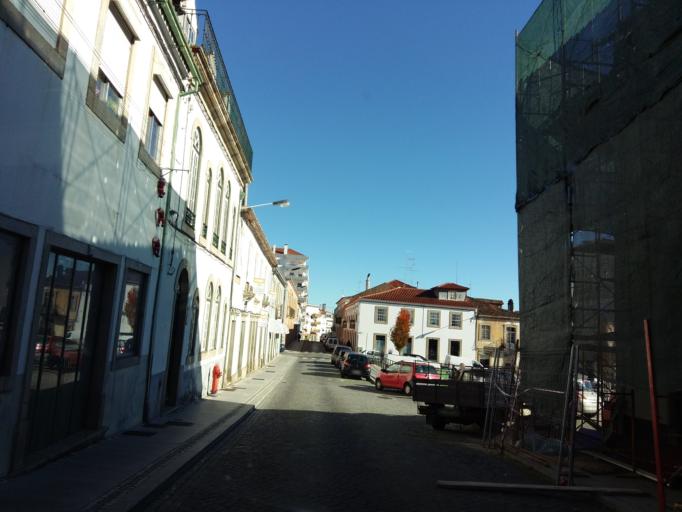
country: PT
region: Castelo Branco
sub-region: Castelo Branco
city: Castelo Branco
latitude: 39.8254
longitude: -7.4902
